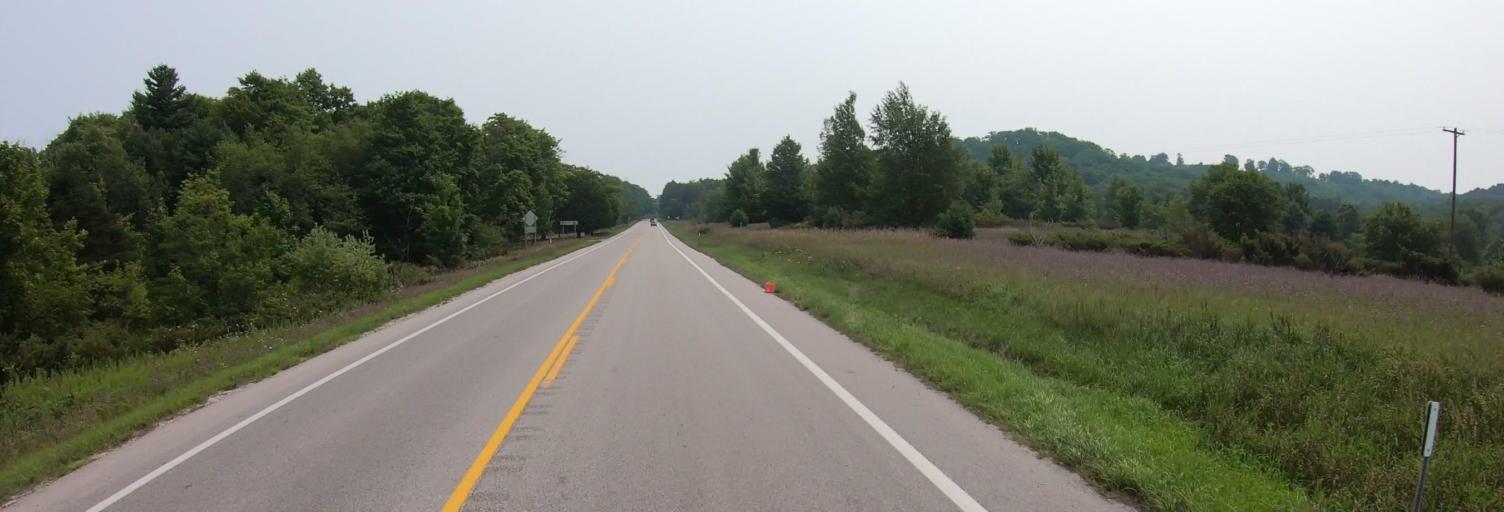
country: US
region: Michigan
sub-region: Leelanau County
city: Leland
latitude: 44.9219
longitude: -85.8716
